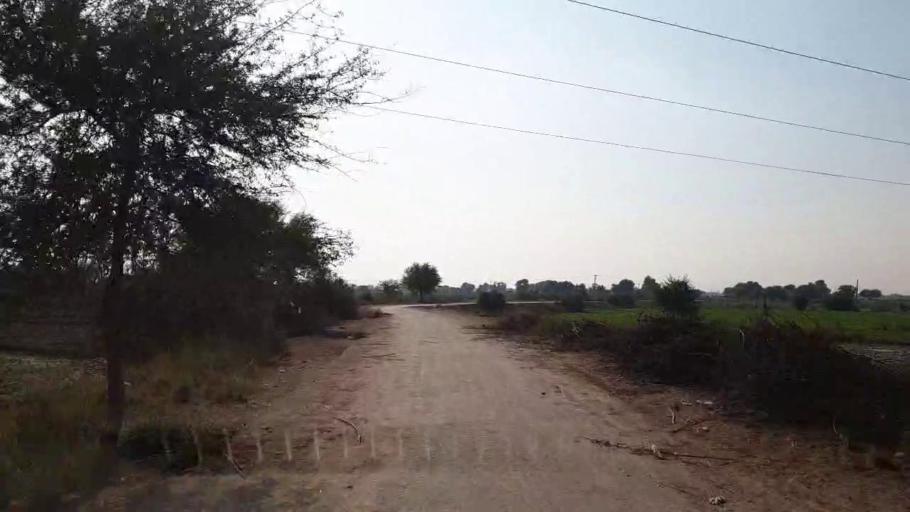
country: PK
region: Sindh
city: Sehwan
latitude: 26.4456
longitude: 67.8135
